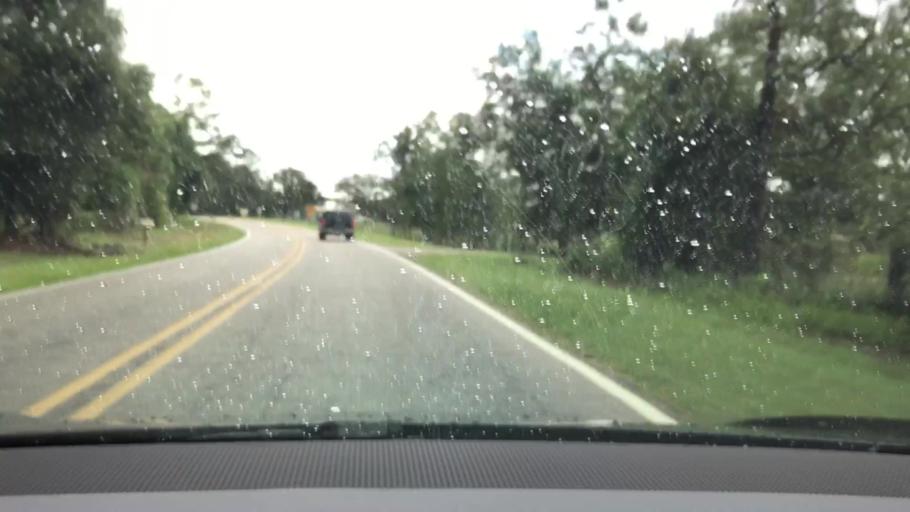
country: US
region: Alabama
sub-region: Geneva County
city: Samson
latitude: 31.1138
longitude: -86.1155
